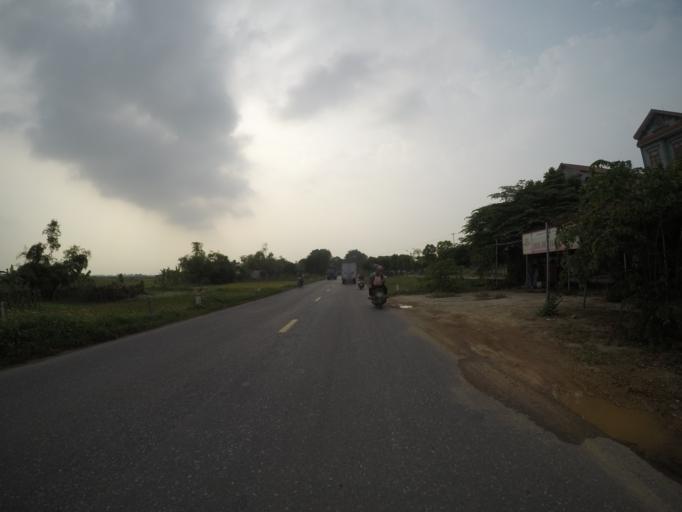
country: VN
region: Ha Noi
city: Soc Son
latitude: 21.2294
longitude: 105.7909
